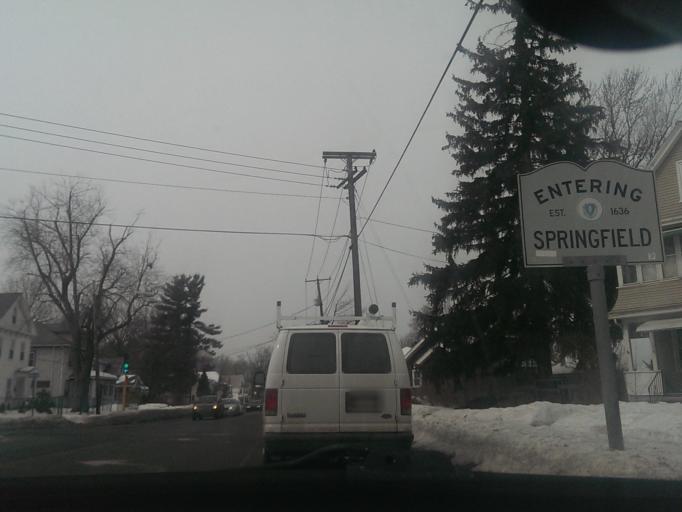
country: US
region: Massachusetts
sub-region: Hampden County
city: East Longmeadow
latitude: 42.0813
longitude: -72.5396
